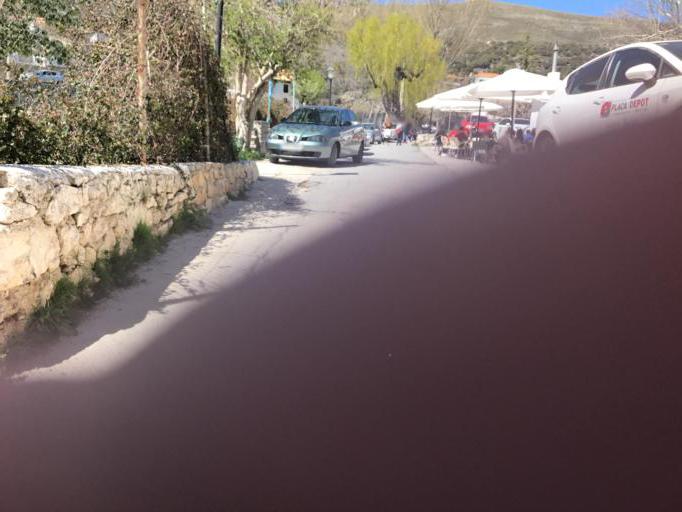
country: ES
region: Andalusia
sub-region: Provincia de Granada
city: Iznalloz
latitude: 37.3215
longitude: -3.4527
